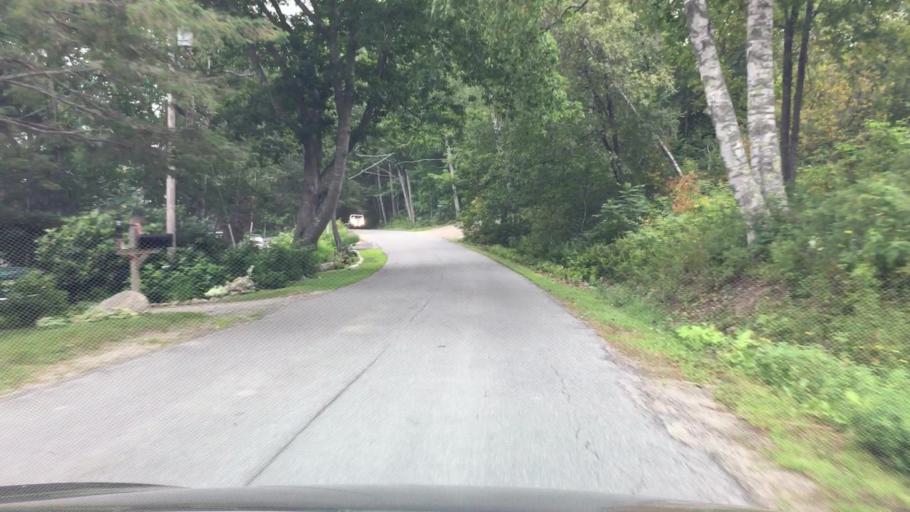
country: US
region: Maine
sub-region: Waldo County
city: Stockton Springs
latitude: 44.5135
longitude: -68.8118
